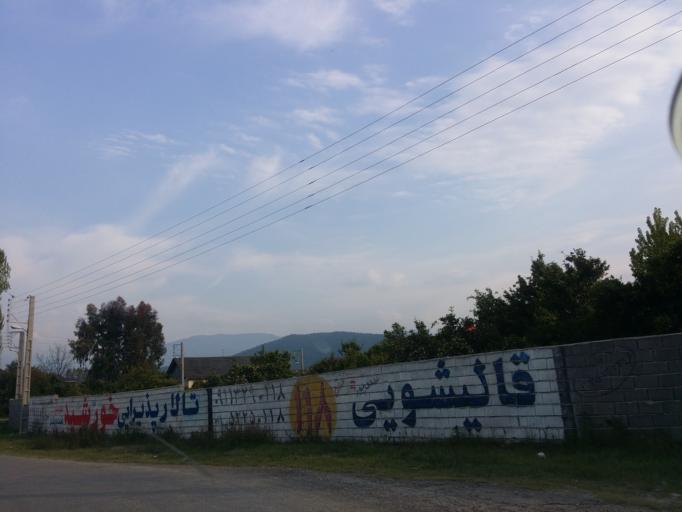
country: IR
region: Mazandaran
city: Chalus
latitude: 36.6725
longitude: 51.3709
